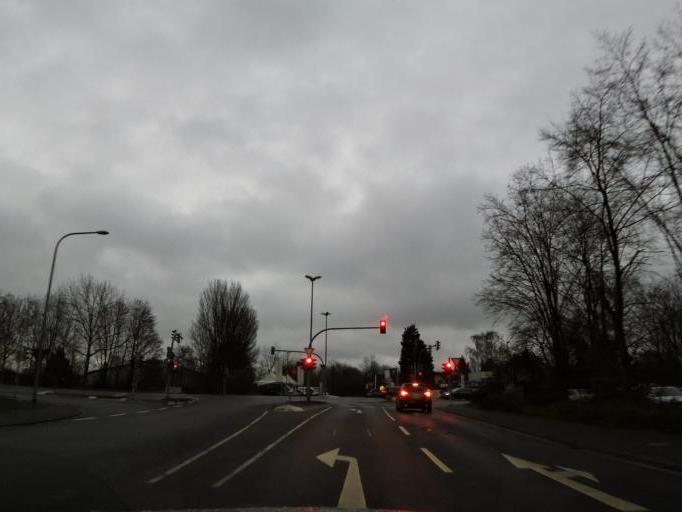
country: DE
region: Hesse
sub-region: Regierungsbezirk Darmstadt
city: Gross-Gerau
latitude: 49.9093
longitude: 8.4851
